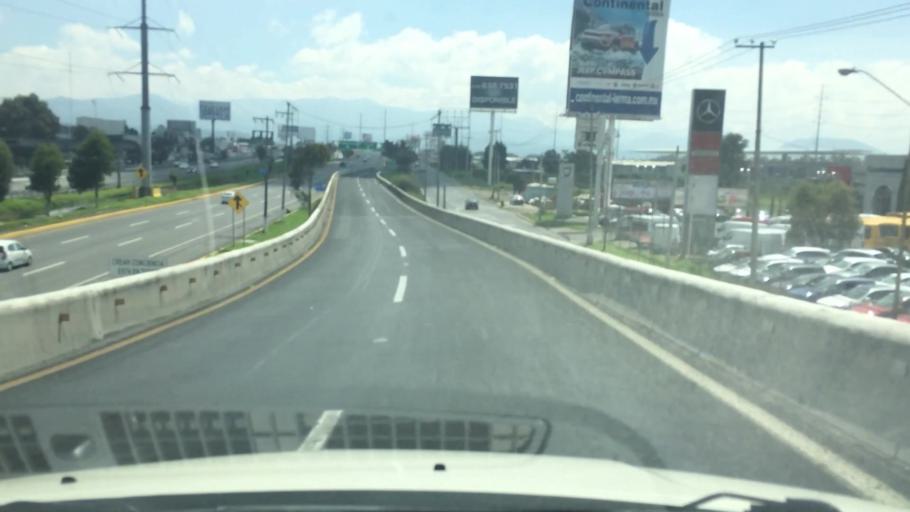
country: MX
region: Morelos
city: Lerma de Villada
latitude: 19.2824
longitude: -99.5201
